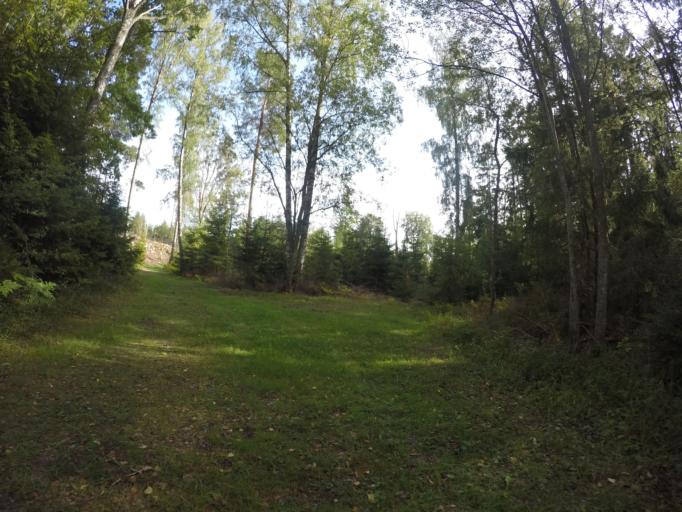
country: SE
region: Soedermanland
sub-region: Eskilstuna Kommun
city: Kvicksund
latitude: 59.5121
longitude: 16.3067
